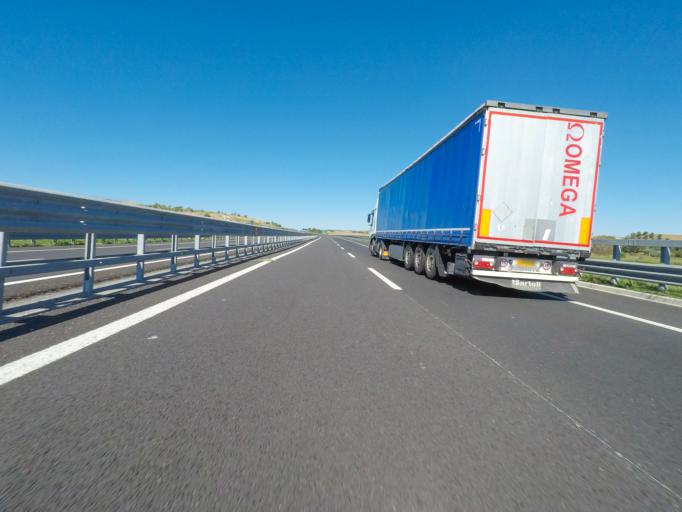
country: IT
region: Latium
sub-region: Provincia di Viterbo
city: Tarquinia
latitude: 42.2009
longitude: 11.7855
